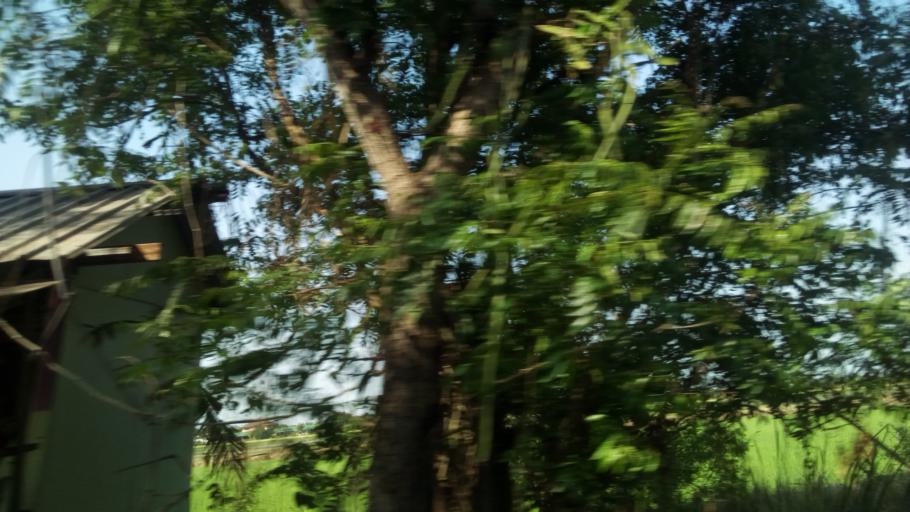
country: TH
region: Nonthaburi
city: Sai Noi
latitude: 13.9415
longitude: 100.3331
